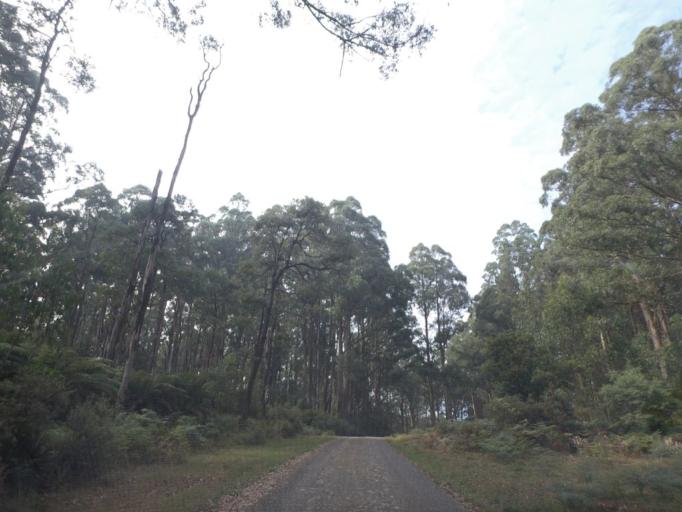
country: AU
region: Victoria
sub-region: Yarra Ranges
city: Healesville
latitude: -37.5726
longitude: 145.5436
